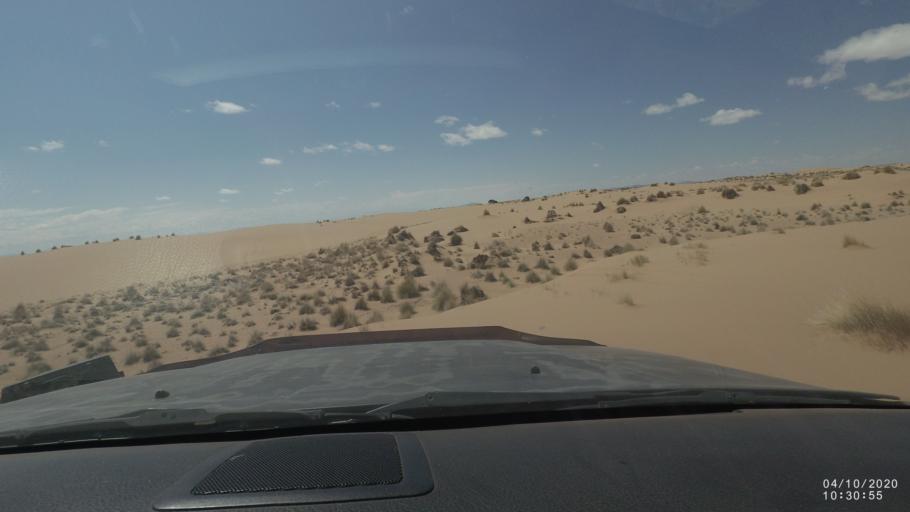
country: BO
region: Oruro
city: Poopo
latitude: -18.7038
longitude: -67.4847
